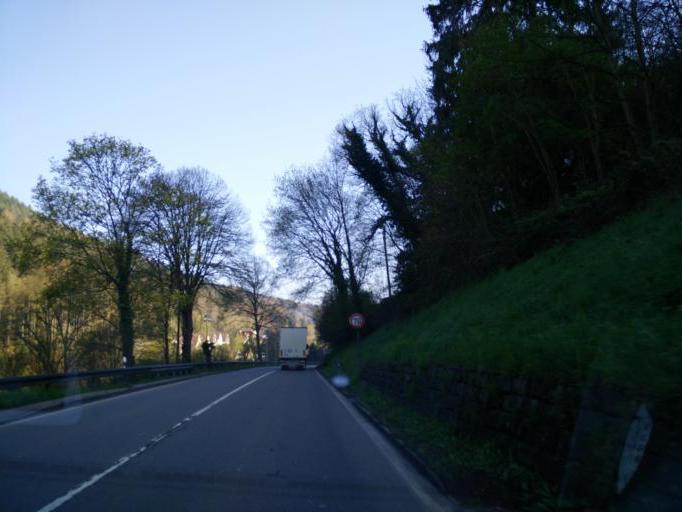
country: DE
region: Baden-Wuerttemberg
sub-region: Karlsruhe Region
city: Calw
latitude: 48.7278
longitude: 8.7336
